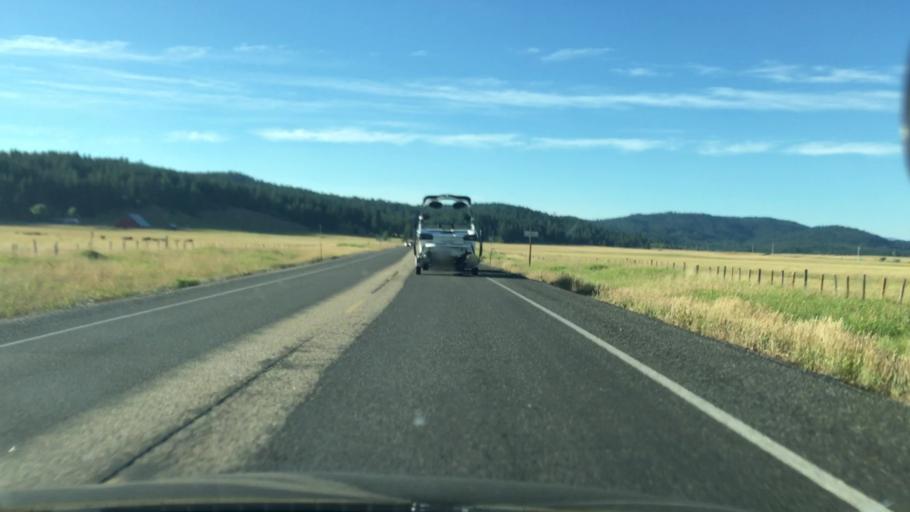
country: US
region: Idaho
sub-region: Valley County
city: Cascade
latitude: 44.5454
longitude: -116.0264
